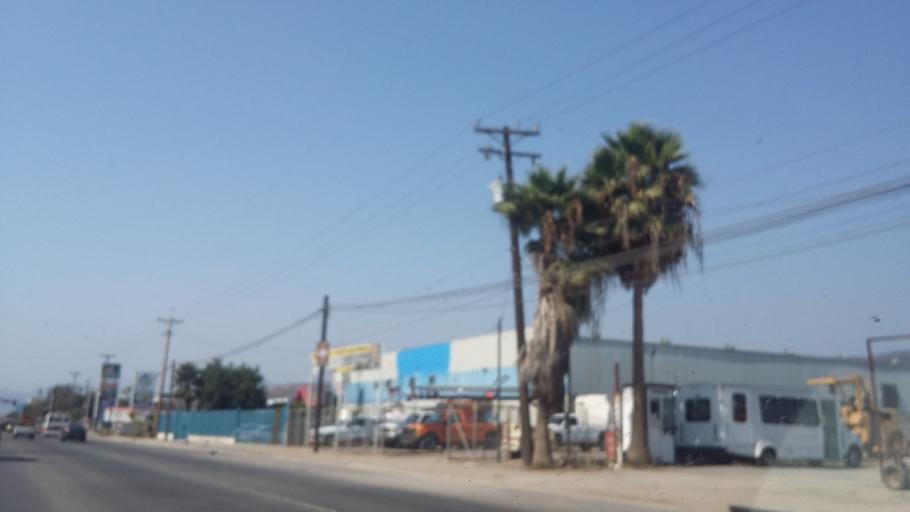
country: MX
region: Baja California
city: Ensenada
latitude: 31.8020
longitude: -116.5950
